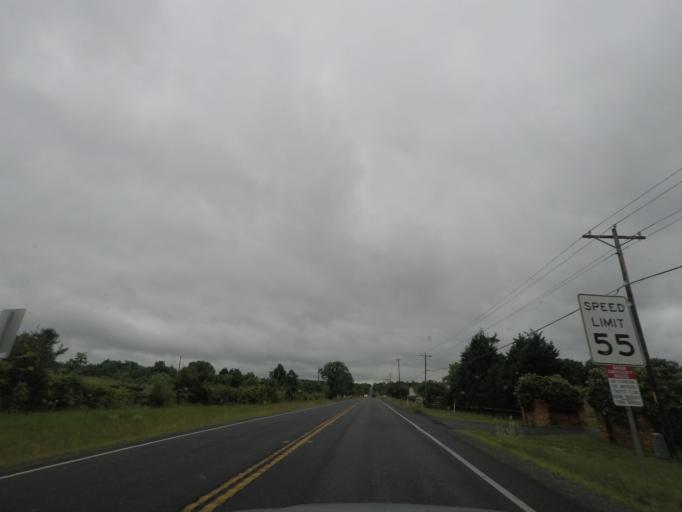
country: US
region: Virginia
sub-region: Prince William County
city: Bull Run Mountain Estates
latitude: 38.8838
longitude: -77.6332
